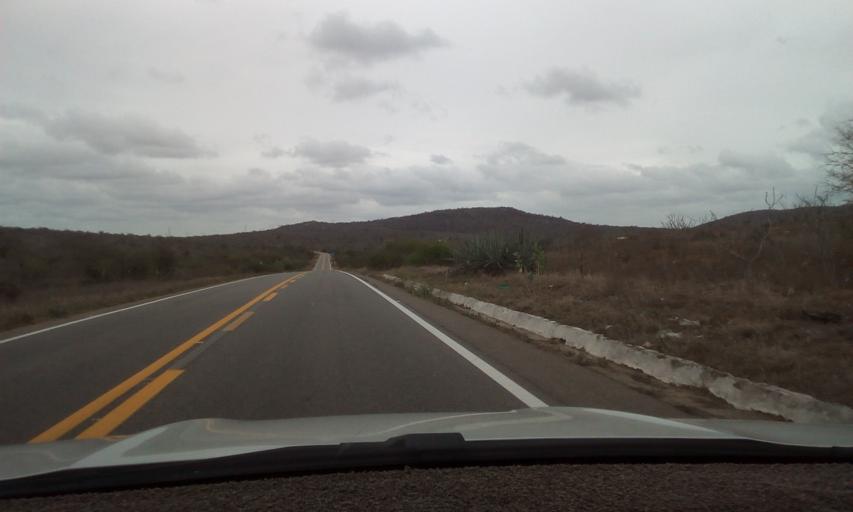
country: BR
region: Paraiba
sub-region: Areia
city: Remigio
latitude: -6.8941
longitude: -35.8988
